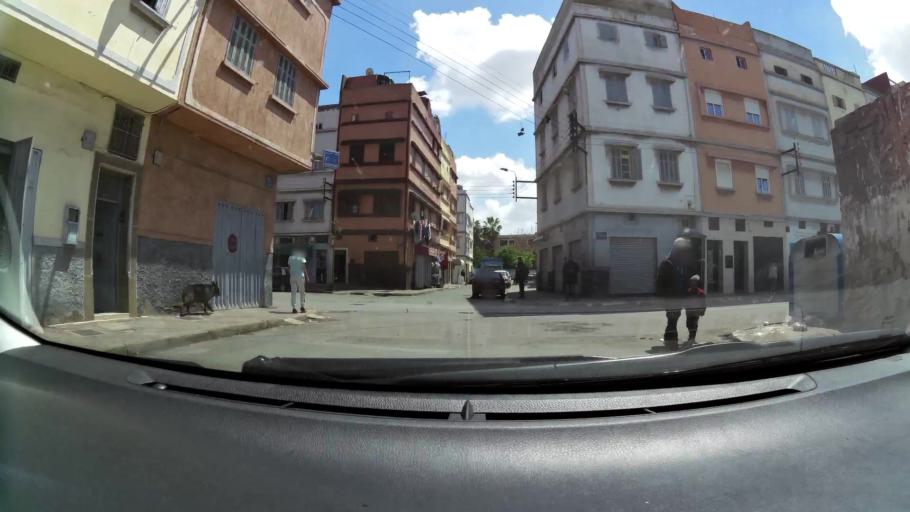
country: MA
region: Grand Casablanca
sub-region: Casablanca
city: Casablanca
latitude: 33.5593
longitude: -7.5859
